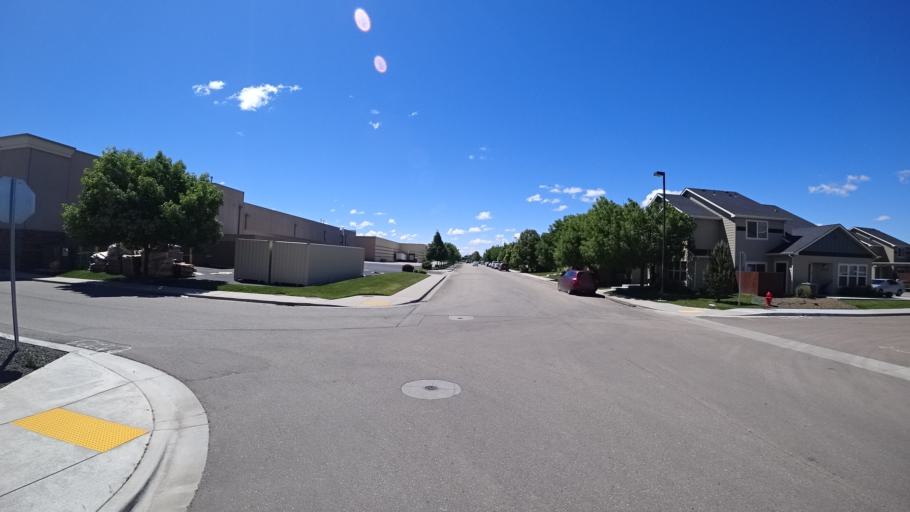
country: US
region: Idaho
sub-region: Ada County
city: Meridian
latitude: 43.6376
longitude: -116.3586
